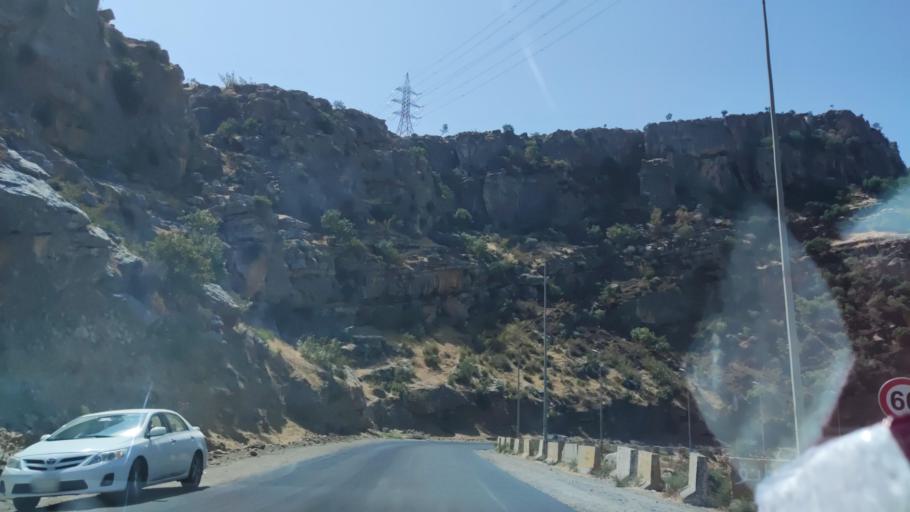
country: IQ
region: Arbil
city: Ruwandiz
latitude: 36.6464
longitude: 44.4967
